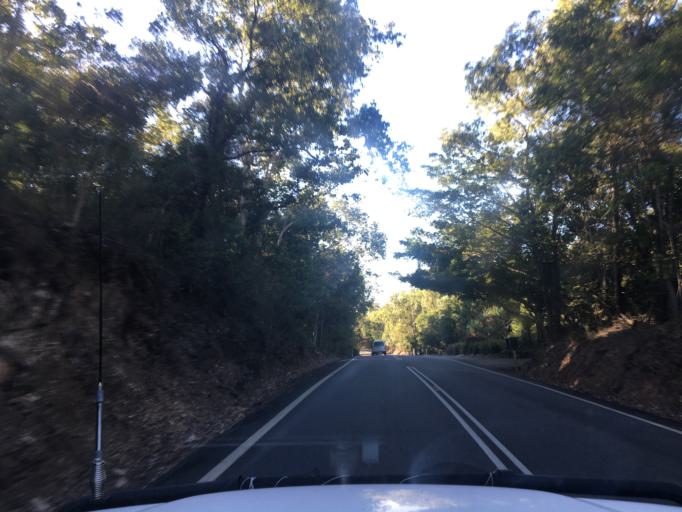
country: AU
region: Queensland
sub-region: Cairns
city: Port Douglas
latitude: -16.5881
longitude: 145.5135
